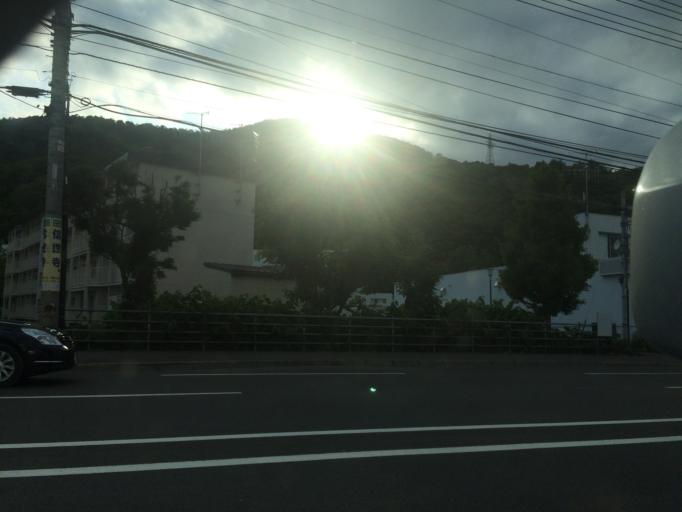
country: JP
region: Hokkaido
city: Sapporo
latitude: 43.0156
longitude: 141.3468
